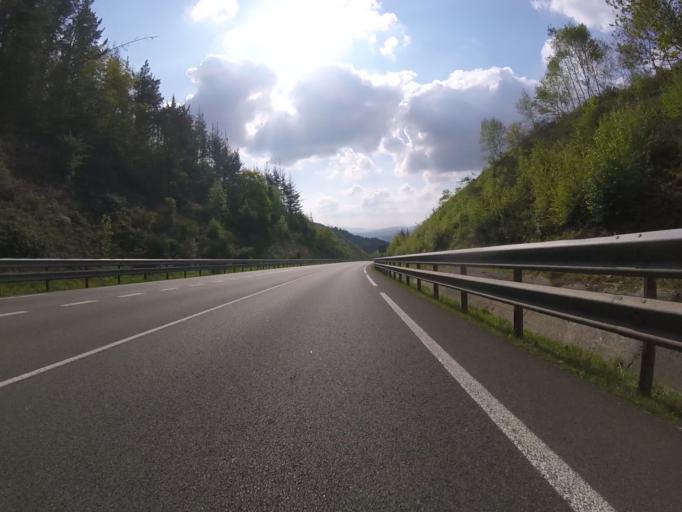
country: ES
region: Basque Country
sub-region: Provincia de Guipuzcoa
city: Azkoitia
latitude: 43.2003
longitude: -2.3442
